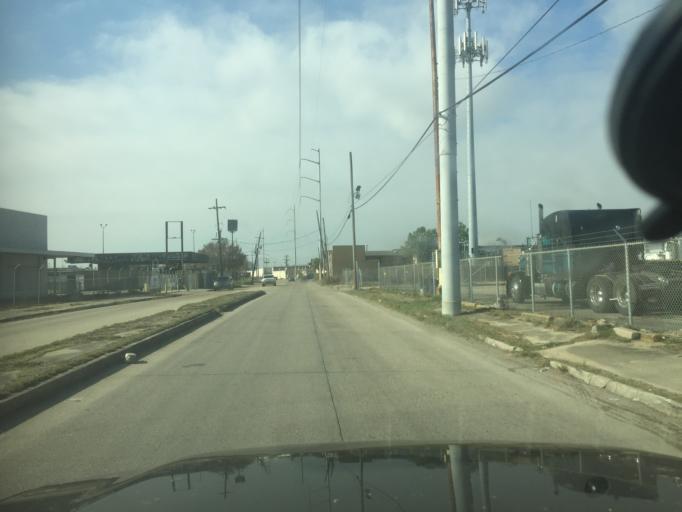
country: US
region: Louisiana
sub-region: Saint Bernard Parish
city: Arabi
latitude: 30.0059
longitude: -90.0301
